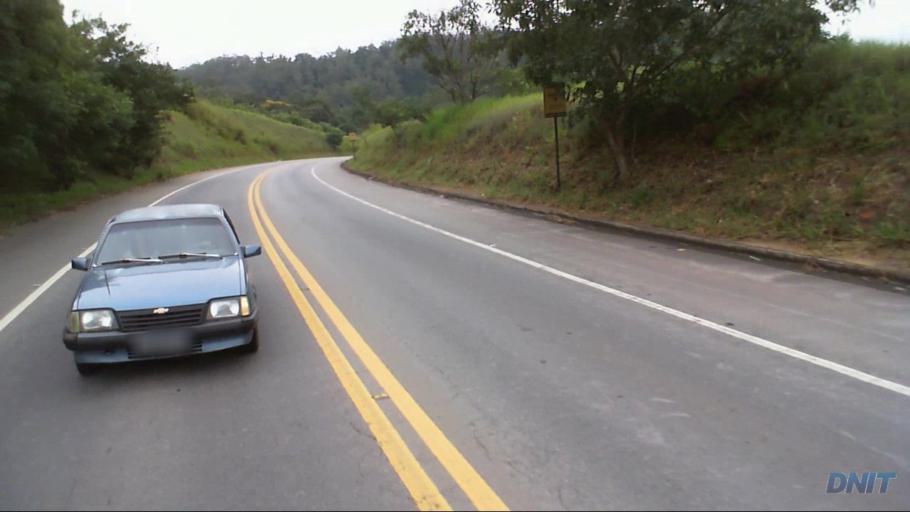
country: BR
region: Minas Gerais
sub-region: Coronel Fabriciano
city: Coronel Fabriciano
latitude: -19.5228
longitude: -42.5815
